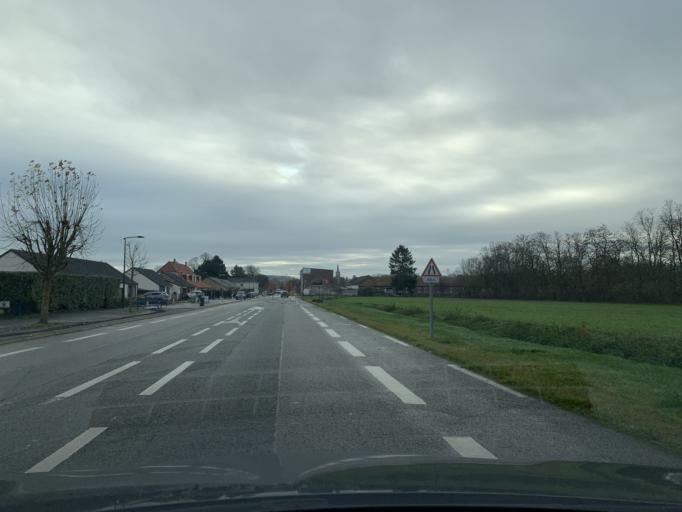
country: FR
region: Nord-Pas-de-Calais
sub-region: Departement du Nord
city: Cantin
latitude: 50.3164
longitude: 3.1194
